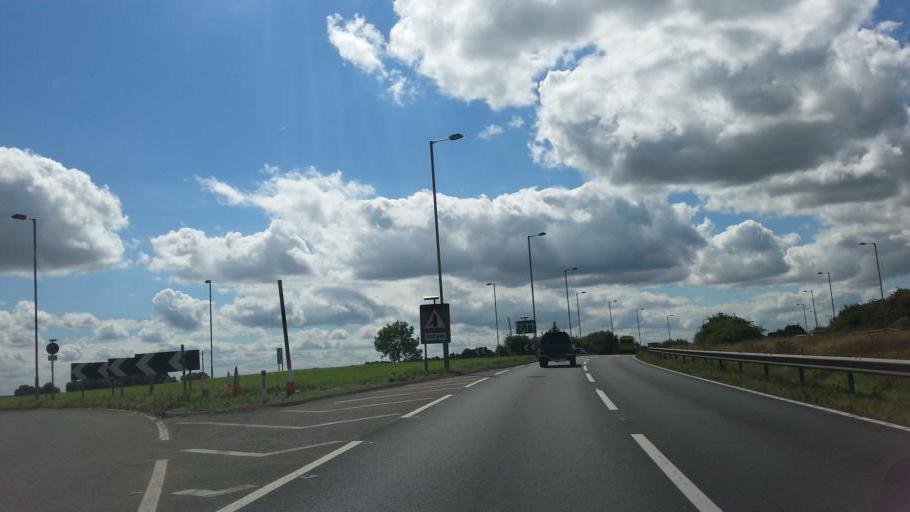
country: GB
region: England
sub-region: Cambridgeshire
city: Buckden
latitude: 52.3035
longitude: -0.2452
